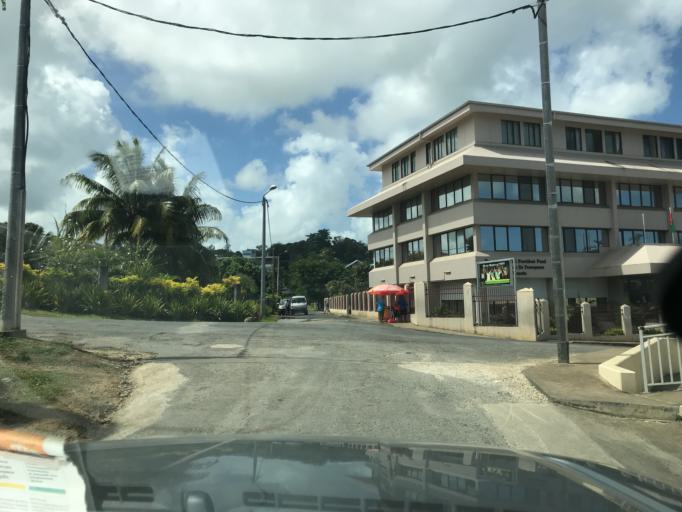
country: VU
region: Shefa
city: Port-Vila
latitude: -17.7346
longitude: 168.3123
